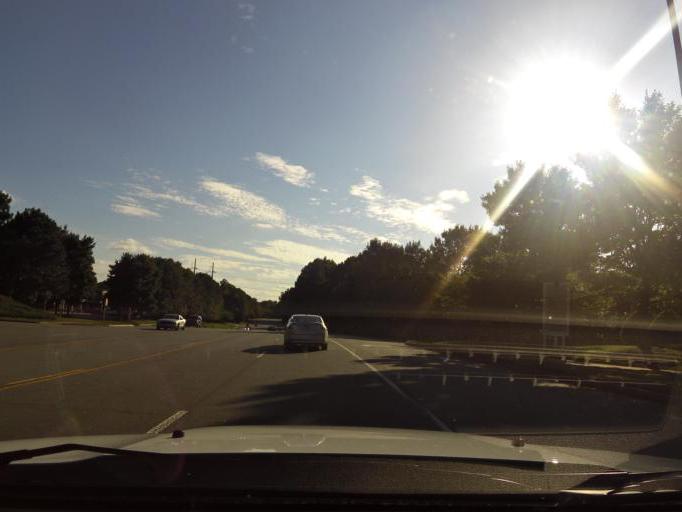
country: US
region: Georgia
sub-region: Cobb County
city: Kennesaw
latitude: 34.0104
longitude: -84.5818
